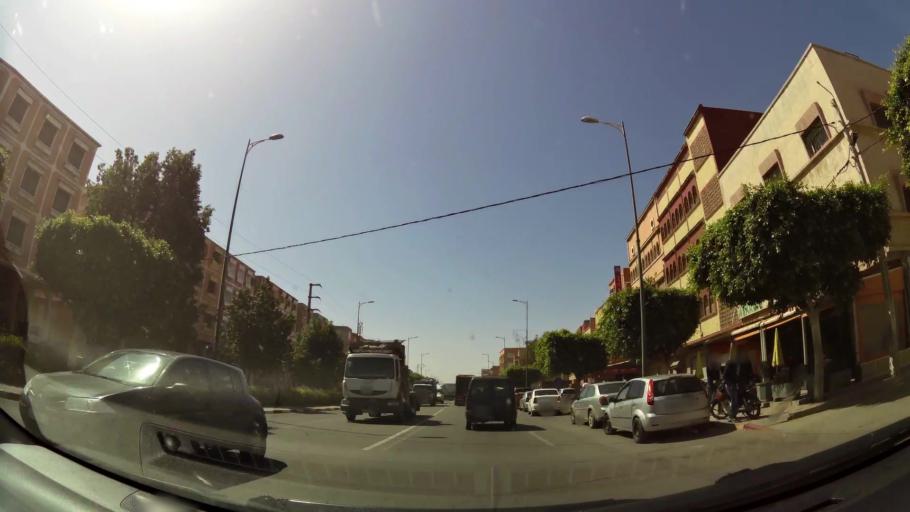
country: MA
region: Souss-Massa-Draa
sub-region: Inezgane-Ait Mellou
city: Inezgane
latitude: 30.3372
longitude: -9.5043
